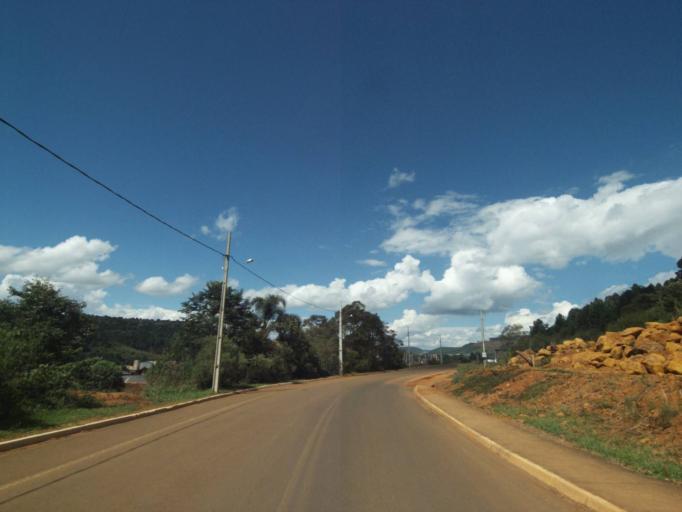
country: BR
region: Parana
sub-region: Uniao Da Vitoria
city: Uniao da Vitoria
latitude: -26.1545
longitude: -51.5507
